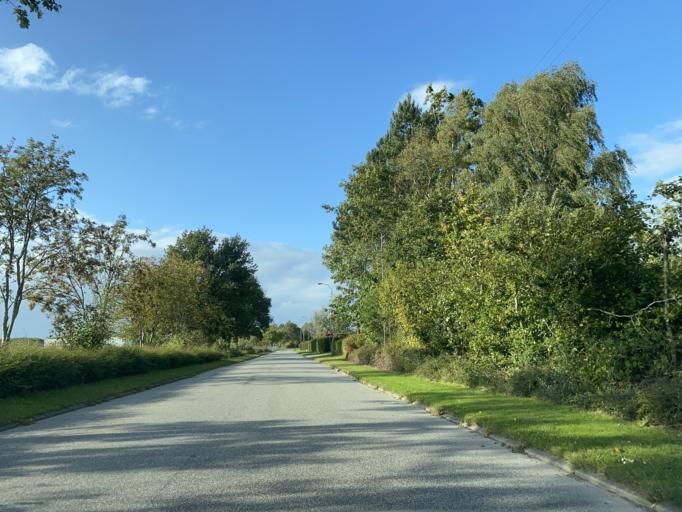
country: DK
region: Central Jutland
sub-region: Skanderborg Kommune
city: Ry
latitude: 56.1509
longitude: 9.8135
